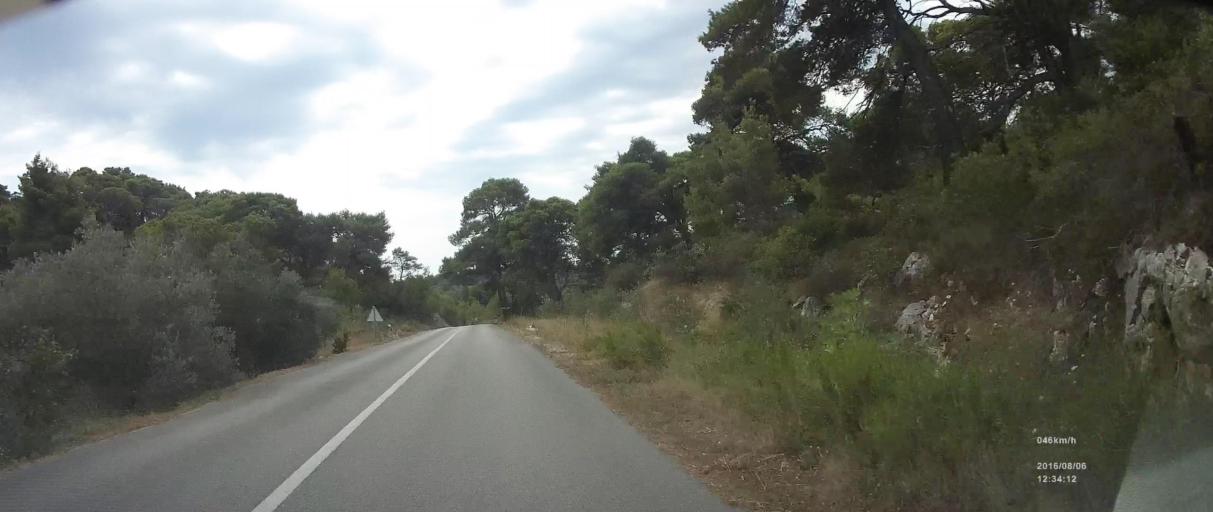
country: HR
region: Dubrovacko-Neretvanska
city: Ston
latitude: 42.7102
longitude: 17.7286
